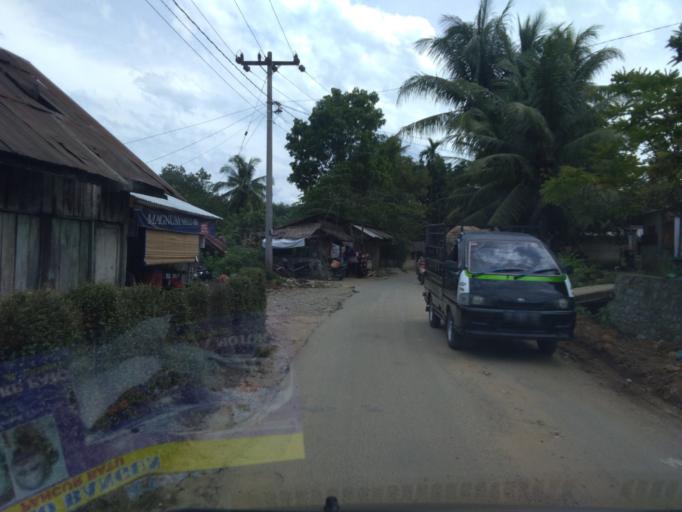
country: ID
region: North Sumatra
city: Deli Tua
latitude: 3.3065
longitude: 98.8104
